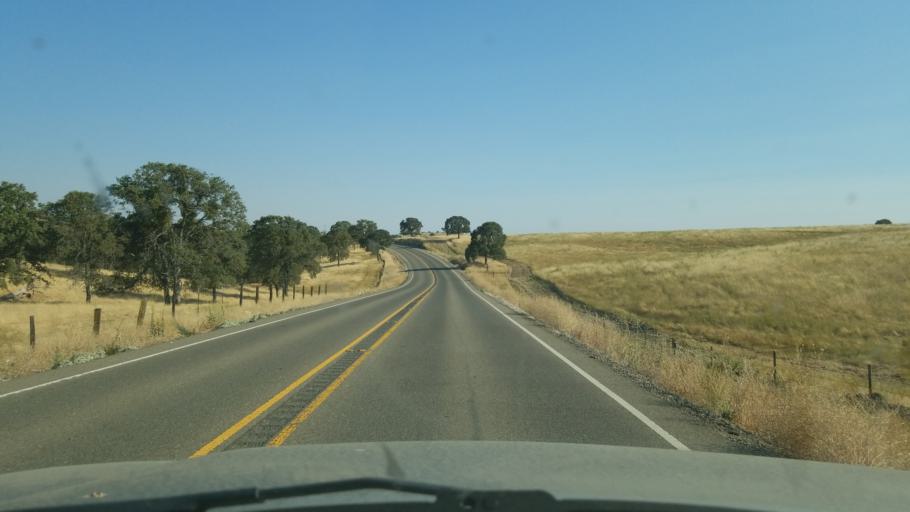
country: US
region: California
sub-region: Tuolumne County
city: Jamestown
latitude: 37.8066
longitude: -120.4727
